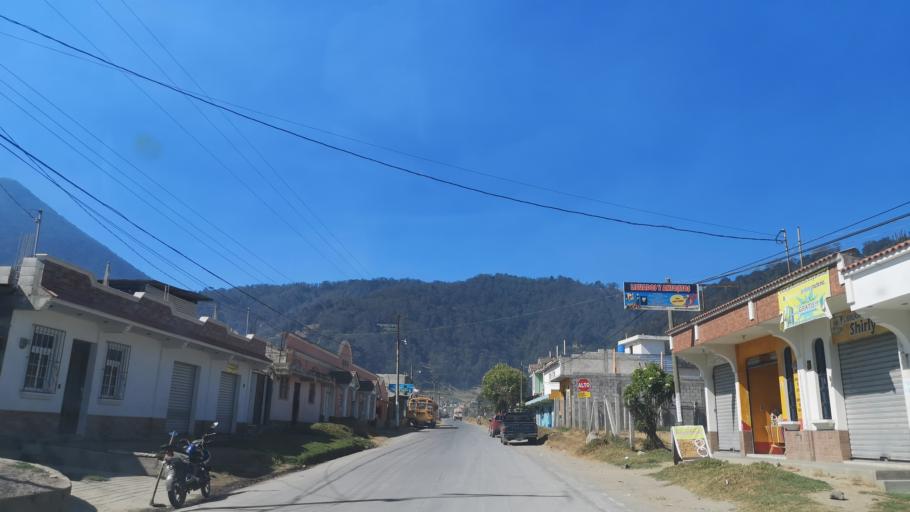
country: GT
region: Quetzaltenango
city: Quetzaltenango
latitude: 14.7978
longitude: -91.5494
